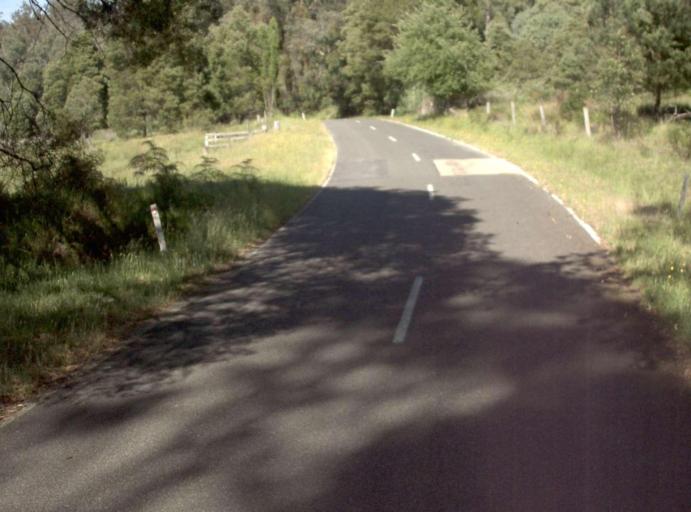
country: AU
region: New South Wales
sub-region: Bombala
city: Bombala
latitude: -37.3441
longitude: 148.6951
